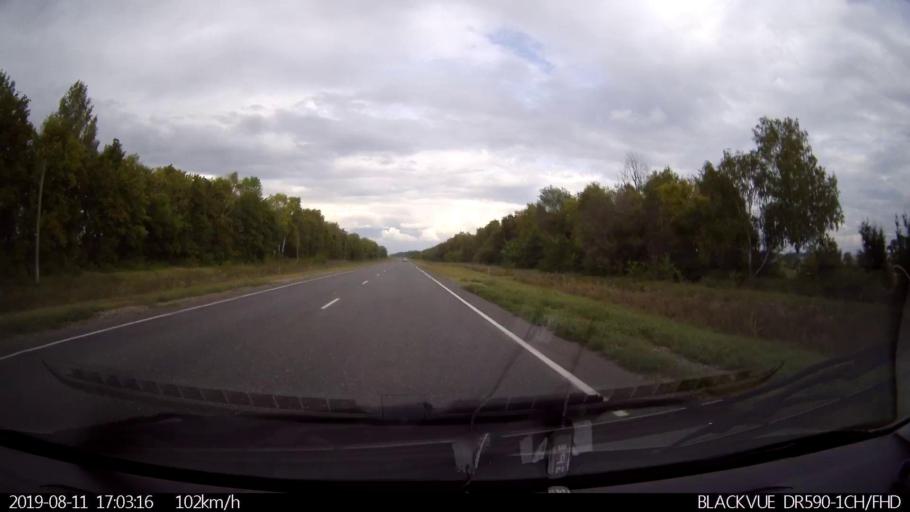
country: RU
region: Ulyanovsk
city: Mayna
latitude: 54.3035
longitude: 47.7355
